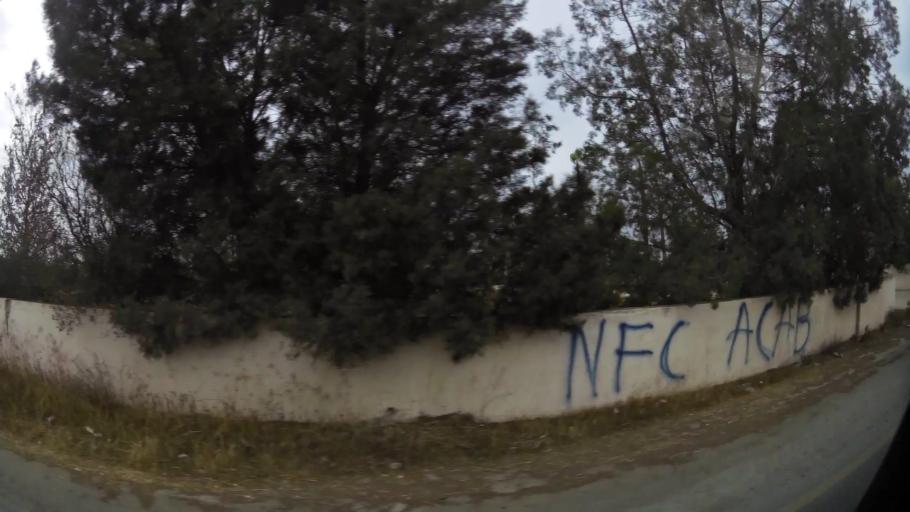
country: CY
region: Lefkosia
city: Geri
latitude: 35.0848
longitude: 33.3954
